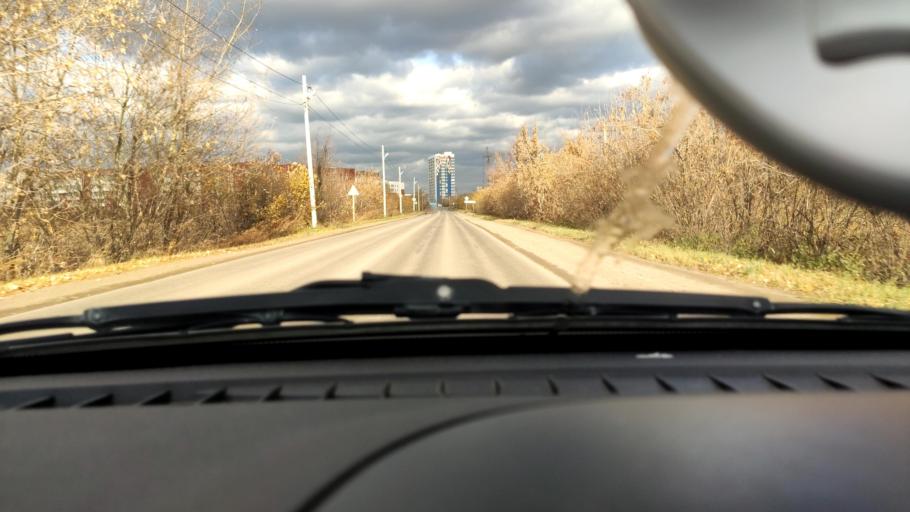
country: RU
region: Perm
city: Kondratovo
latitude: 57.9714
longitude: 56.1134
